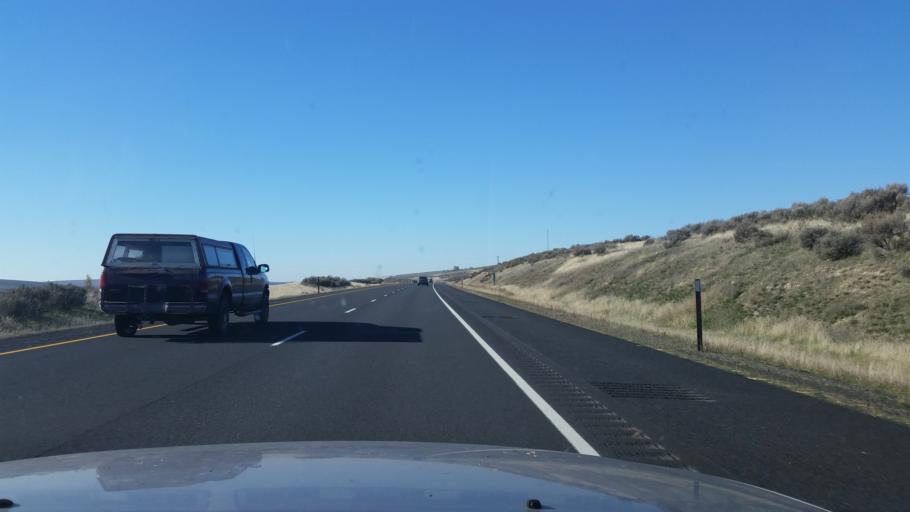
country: US
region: Washington
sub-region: Grant County
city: Warden
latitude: 47.0877
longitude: -118.9141
